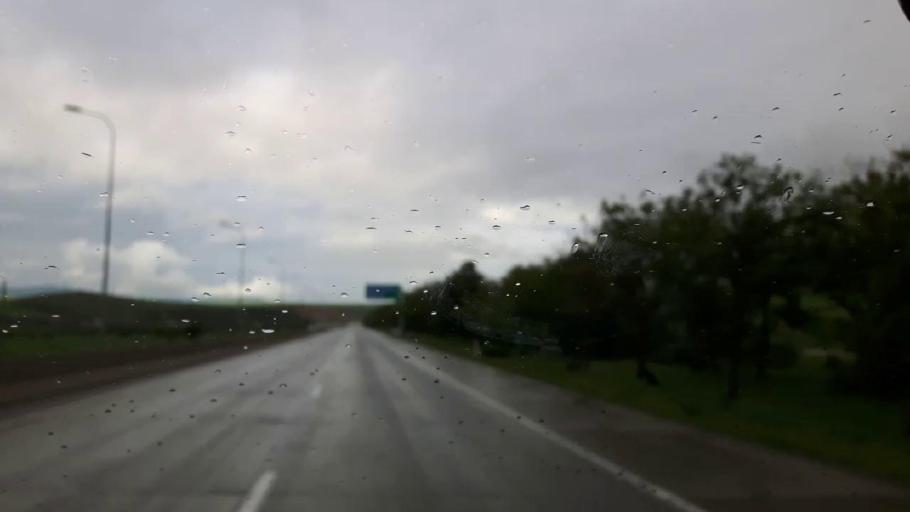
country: GE
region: Shida Kartli
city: Kaspi
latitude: 42.0024
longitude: 44.3761
